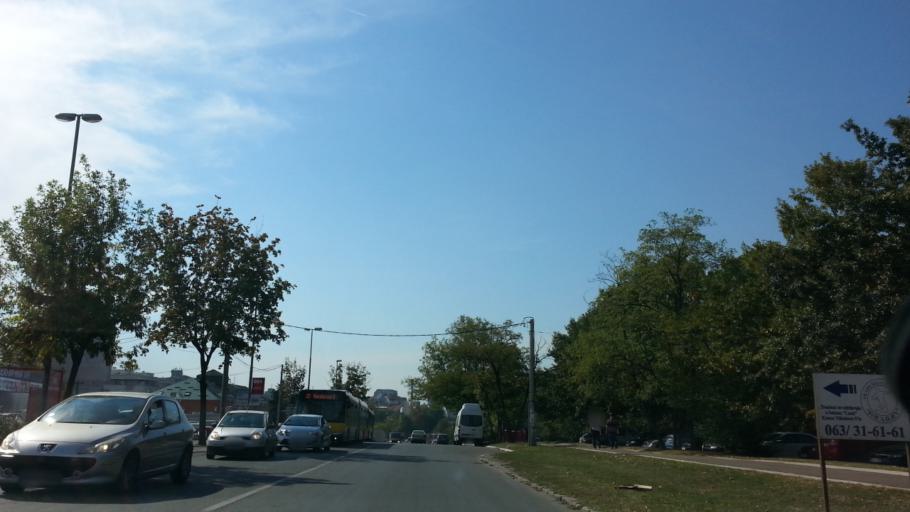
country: RS
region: Central Serbia
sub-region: Belgrade
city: Rakovica
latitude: 44.7460
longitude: 20.4280
